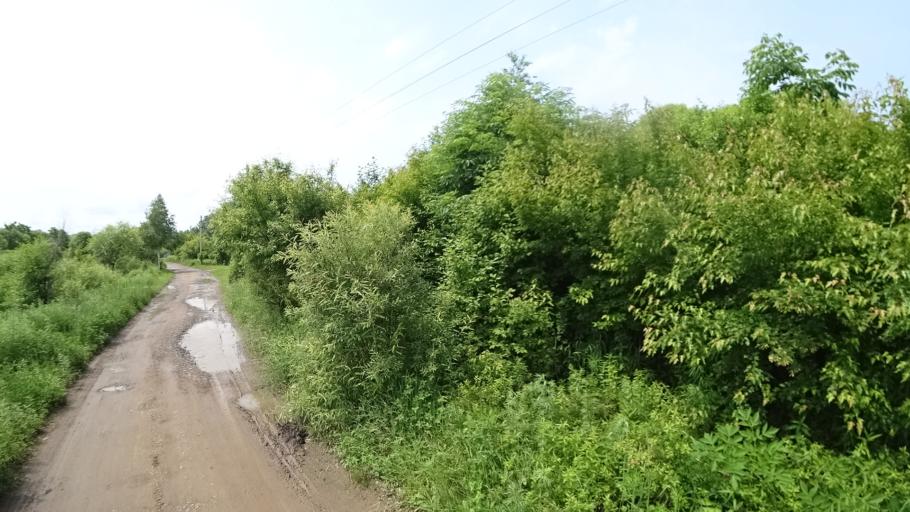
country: RU
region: Primorskiy
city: Novosysoyevka
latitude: 44.2508
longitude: 133.3735
